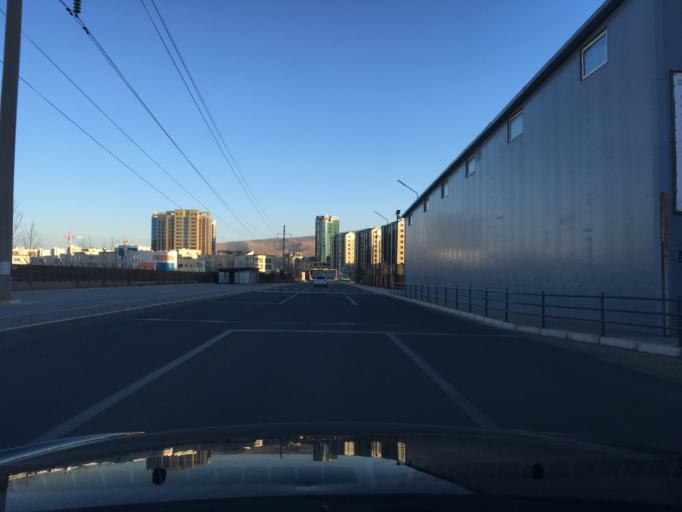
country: MN
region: Ulaanbaatar
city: Ulaanbaatar
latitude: 47.8921
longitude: 106.9266
